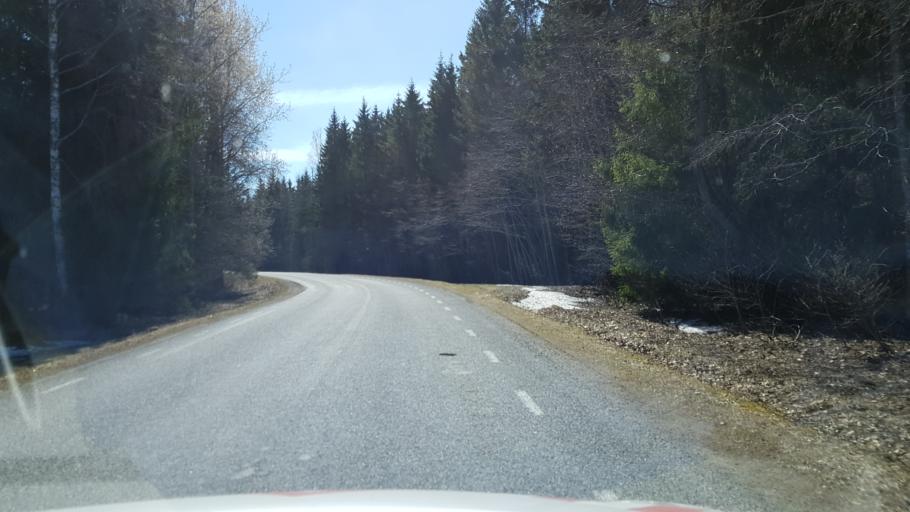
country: EE
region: Laeaene-Virumaa
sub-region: Vinni vald
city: Vinni
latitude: 59.1799
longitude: 26.5015
